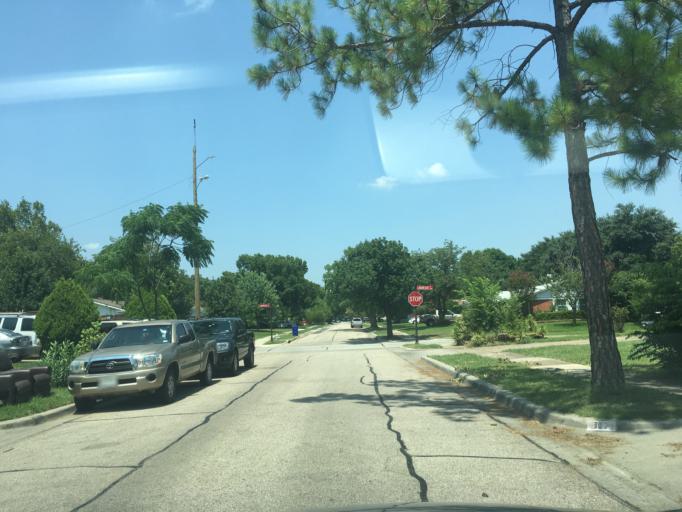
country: US
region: Texas
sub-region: Dallas County
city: Farmers Branch
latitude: 32.9314
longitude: -96.8813
